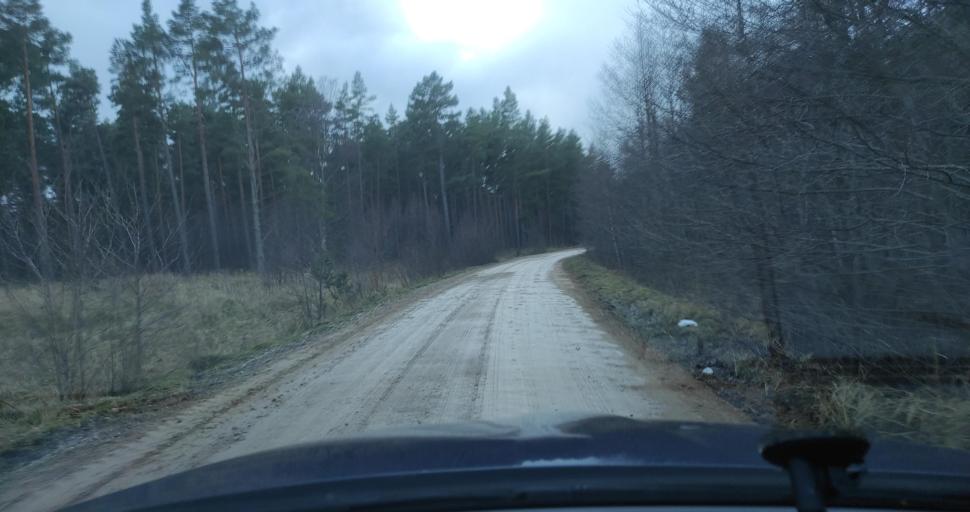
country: LV
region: Pavilostas
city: Pavilosta
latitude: 56.8400
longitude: 21.0832
